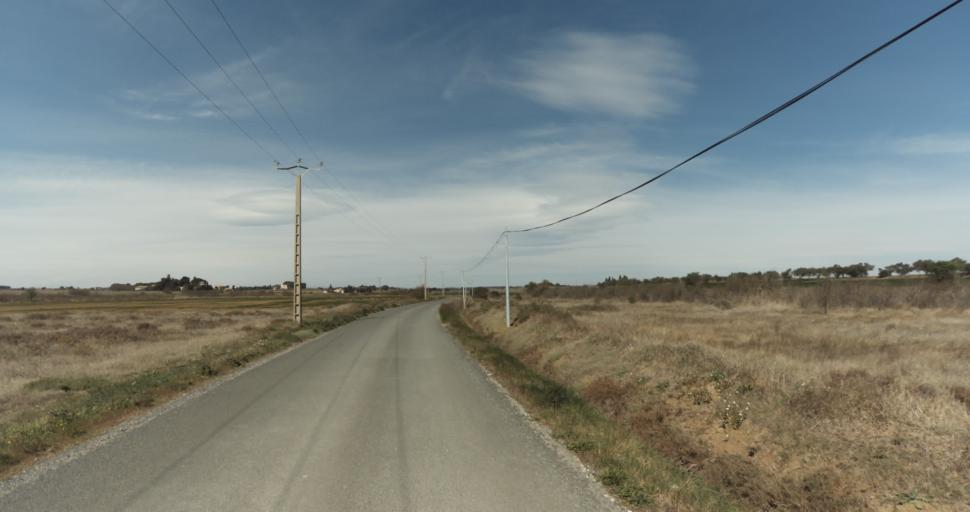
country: FR
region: Languedoc-Roussillon
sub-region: Departement de l'Herault
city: Marseillan
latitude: 43.3836
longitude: 3.5535
